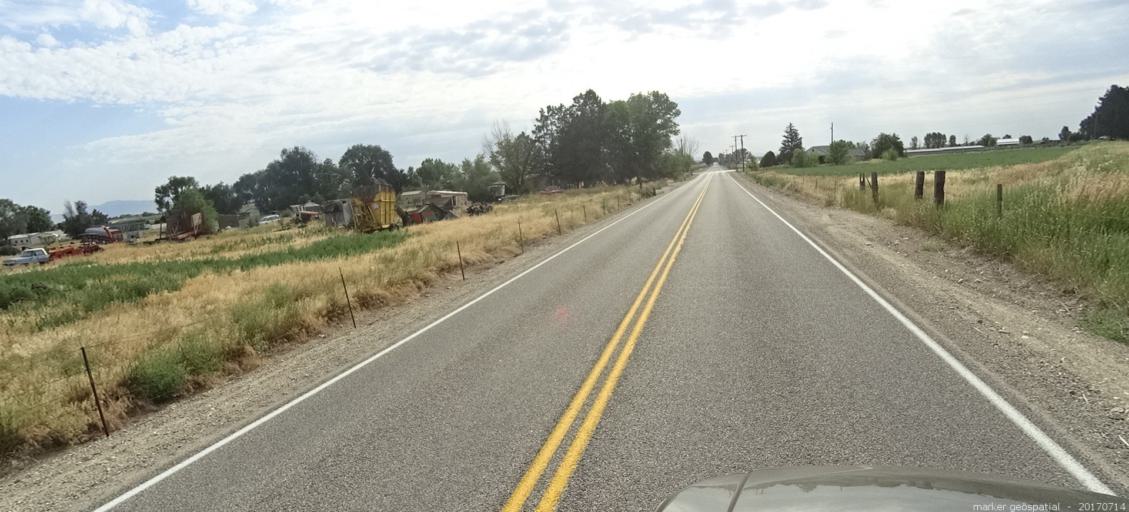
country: US
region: Idaho
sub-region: Ada County
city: Kuna
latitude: 43.4736
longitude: -116.3568
